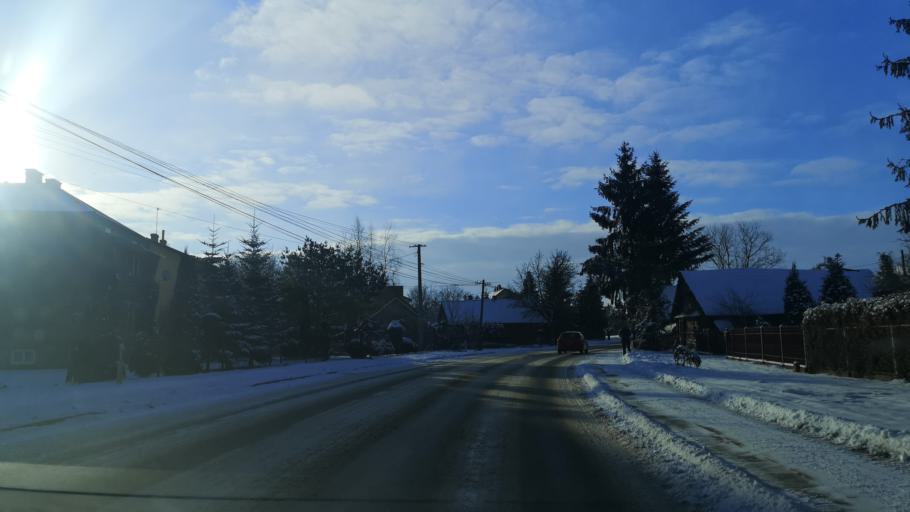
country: PL
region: Subcarpathian Voivodeship
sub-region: Powiat przeworski
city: Gorliczyna
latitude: 50.0940
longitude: 22.4920
